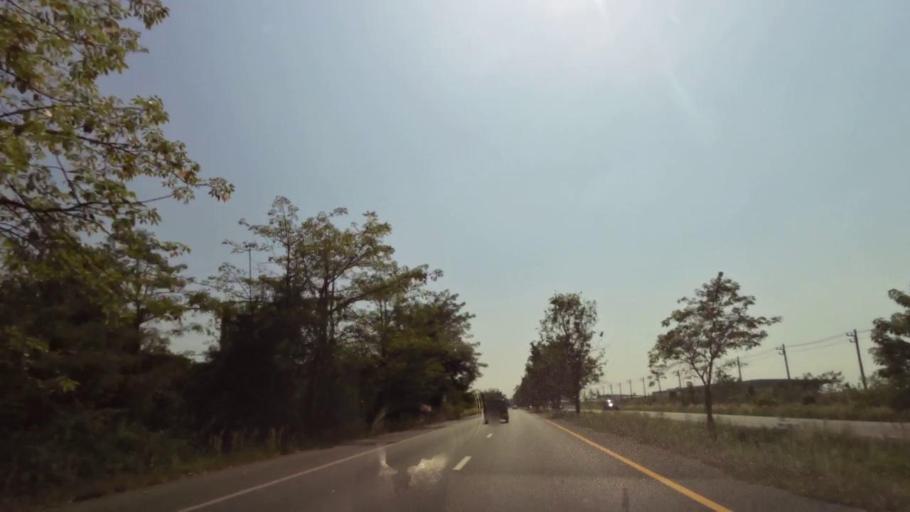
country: TH
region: Nakhon Sawan
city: Kao Liao
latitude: 15.9364
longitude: 100.1131
